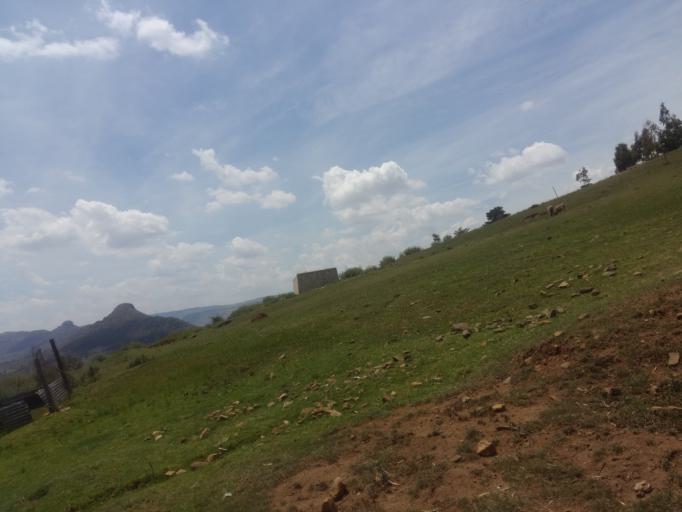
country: LS
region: Mafeteng
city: Mafeteng
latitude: -29.7037
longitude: 27.4351
